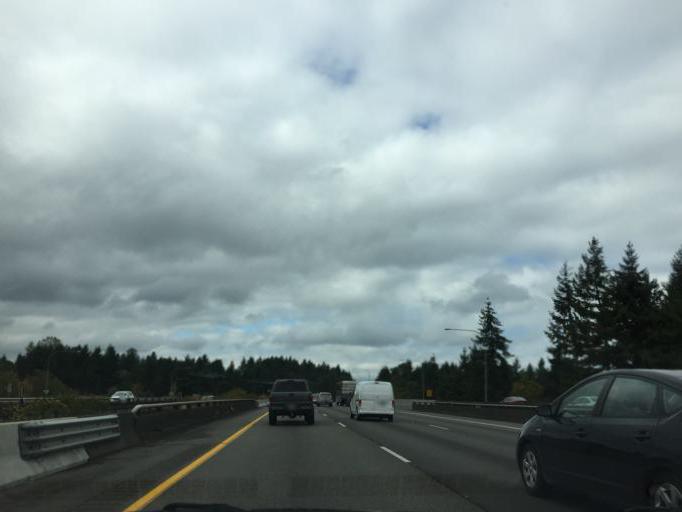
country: US
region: Washington
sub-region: Pierce County
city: Fort Lewis
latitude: 47.1044
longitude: -122.5880
